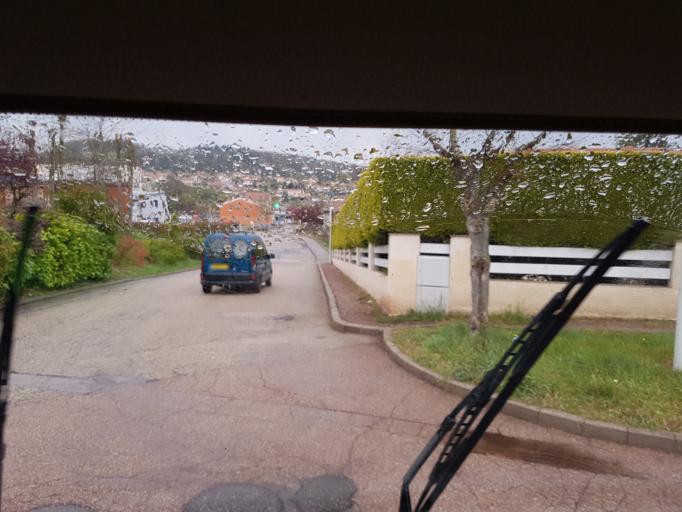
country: FR
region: Rhone-Alpes
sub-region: Departement de la Loire
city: La Ricamarie
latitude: 45.4224
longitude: 4.3183
